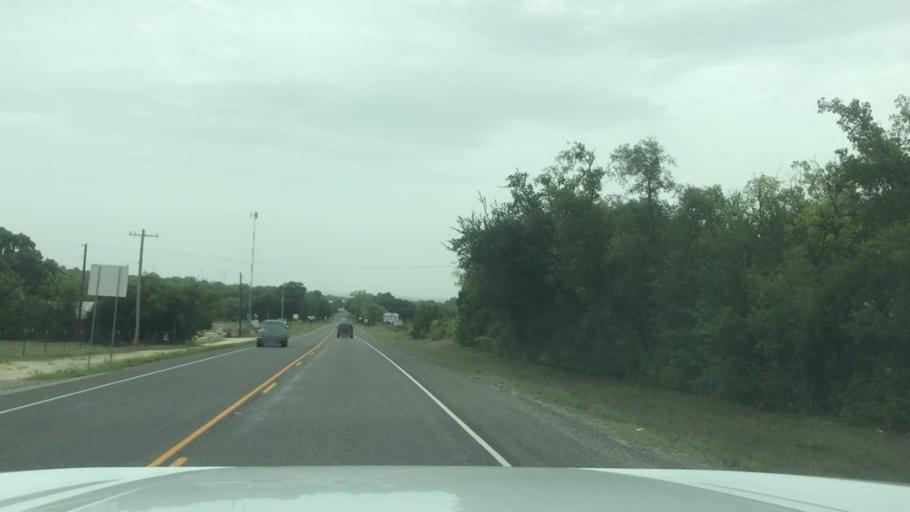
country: US
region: Texas
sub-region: Hamilton County
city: Hico
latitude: 31.9934
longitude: -98.0441
